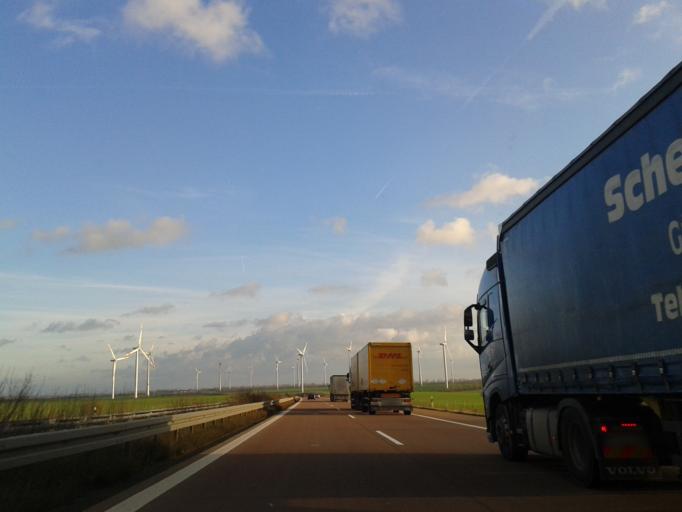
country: DE
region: Saxony-Anhalt
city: Obhausen
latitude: 51.4095
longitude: 11.6829
